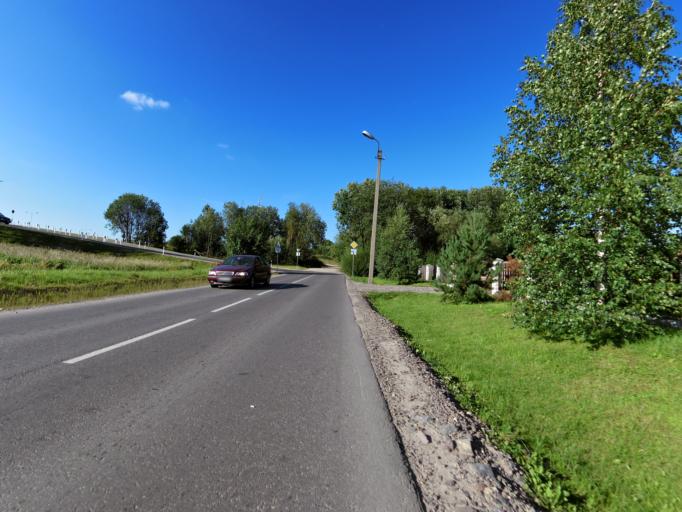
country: LT
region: Vilnius County
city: Justiniskes
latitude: 54.7241
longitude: 25.2100
